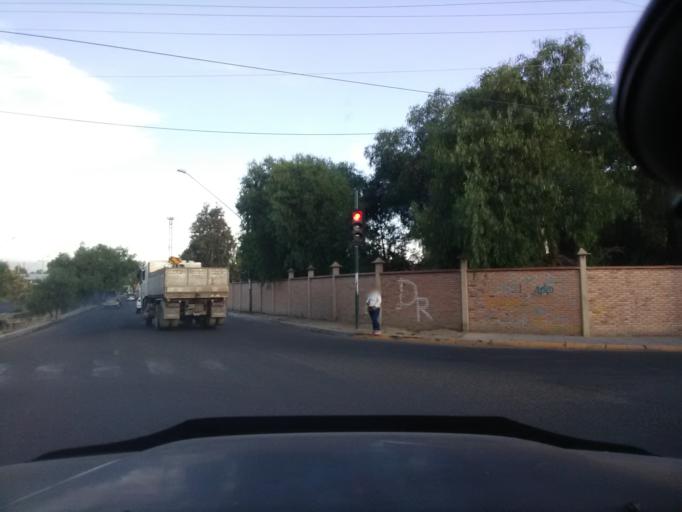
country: BO
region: Cochabamba
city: Cochabamba
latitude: -17.3814
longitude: -66.1990
